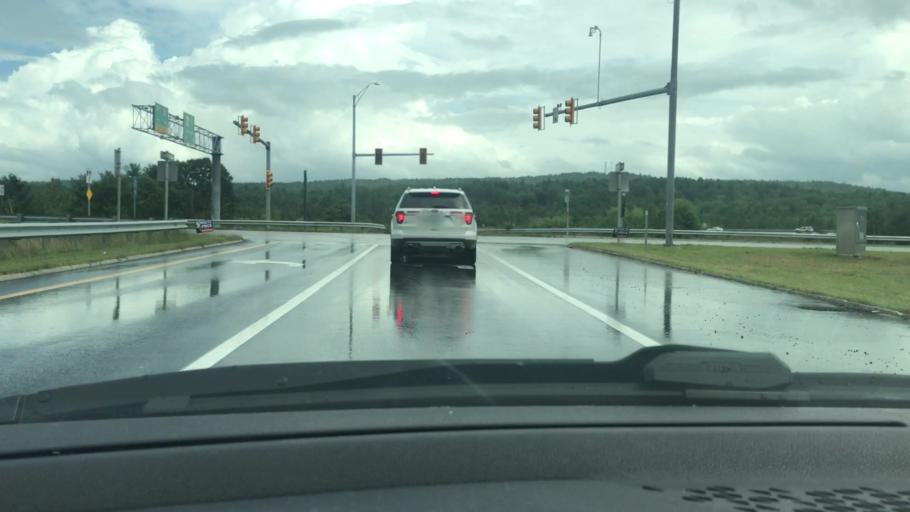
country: US
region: New Hampshire
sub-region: Merrimack County
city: East Concord
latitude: 43.2345
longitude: -71.4712
